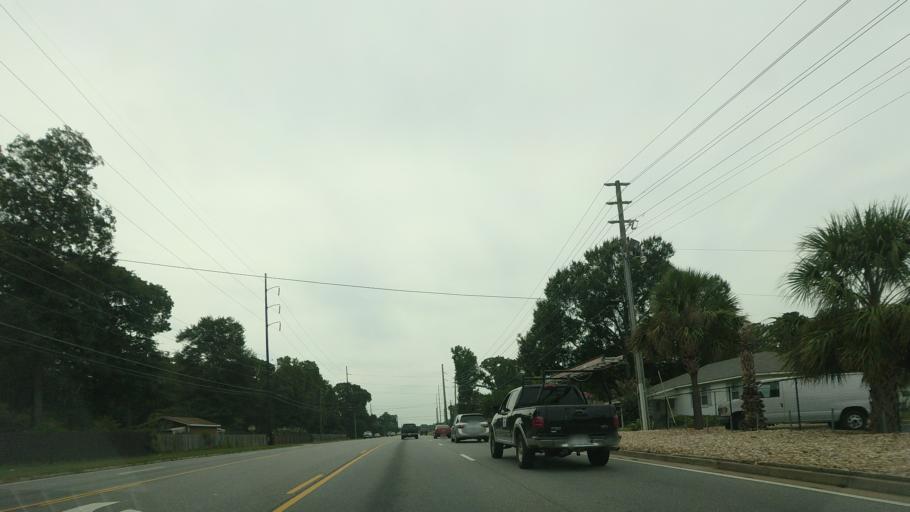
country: US
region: Georgia
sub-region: Houston County
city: Centerville
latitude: 32.5976
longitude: -83.6708
